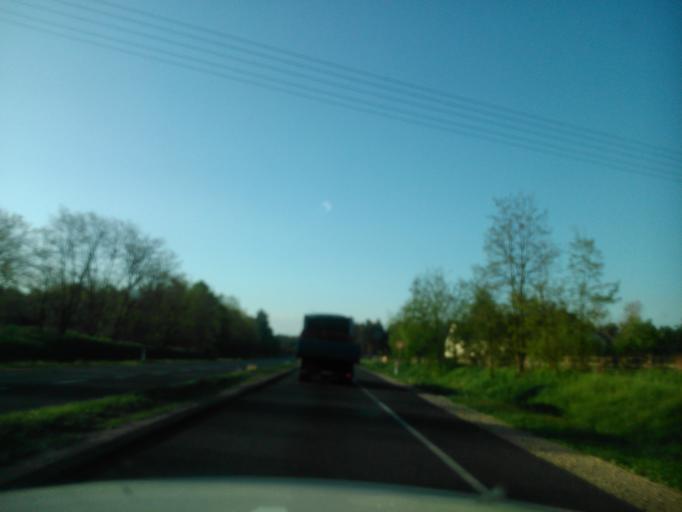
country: PL
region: Masovian Voivodeship
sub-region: Powiat plocki
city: Wyszogrod
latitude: 52.3670
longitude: 20.1925
